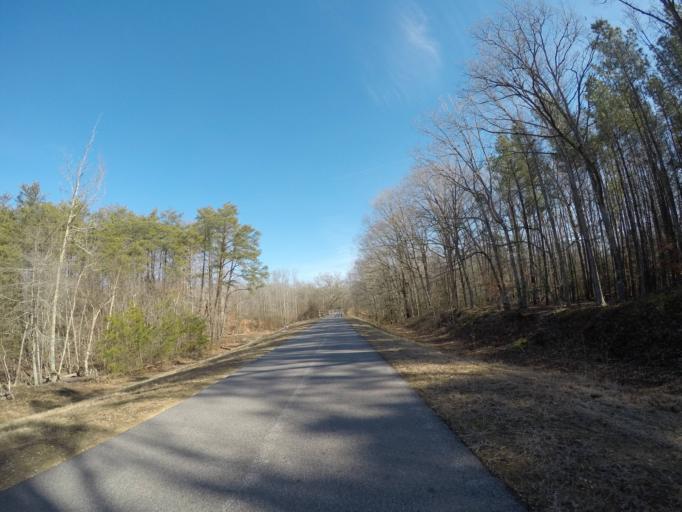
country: US
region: Maryland
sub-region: Charles County
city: Saint Charles
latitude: 38.5970
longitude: -76.9565
